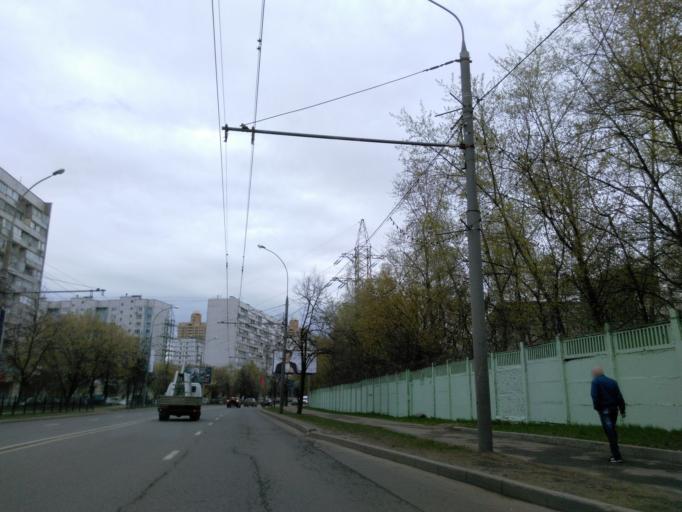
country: RU
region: Moskovskaya
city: Levoberezhnyy
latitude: 55.8437
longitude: 37.4550
